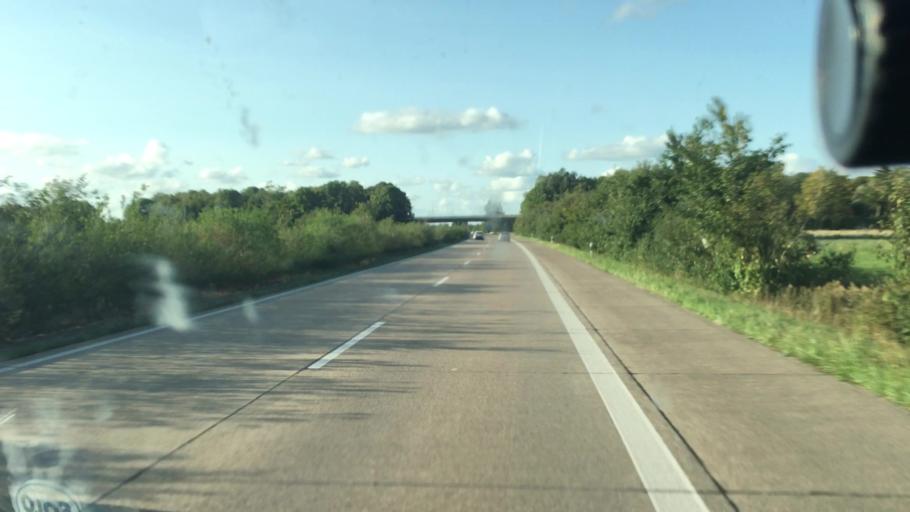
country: DE
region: Lower Saxony
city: Sande
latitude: 53.4717
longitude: 8.0161
